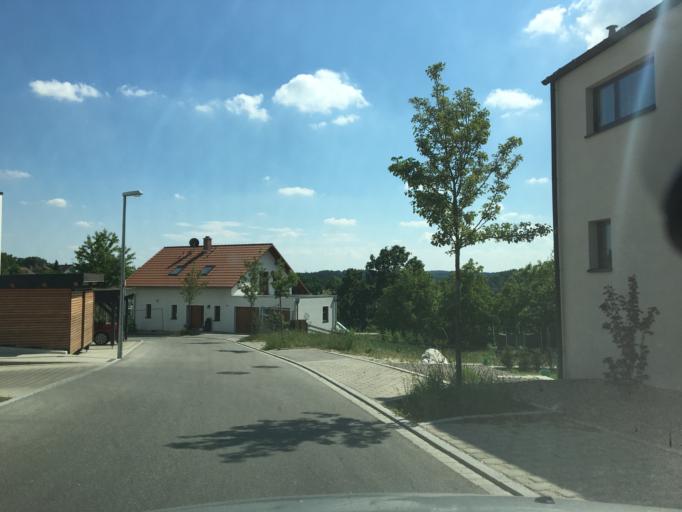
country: DE
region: Bavaria
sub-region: Lower Bavaria
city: Landshut
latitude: 48.5194
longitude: 12.1538
